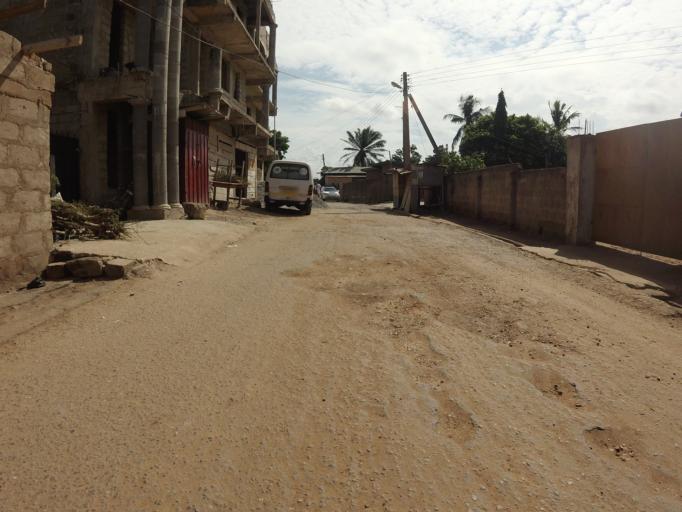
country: GH
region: Greater Accra
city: Accra
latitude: 5.5945
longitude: -0.1909
